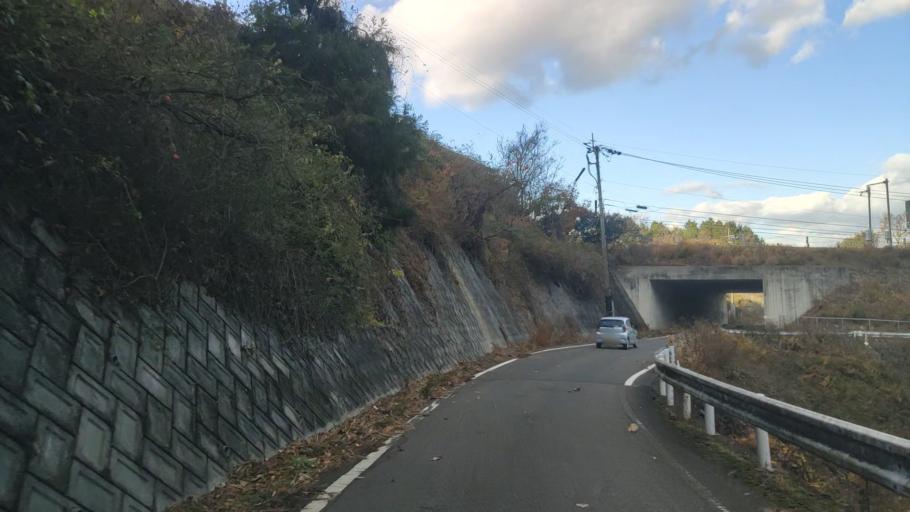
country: JP
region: Ehime
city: Saijo
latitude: 33.8829
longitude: 133.1298
